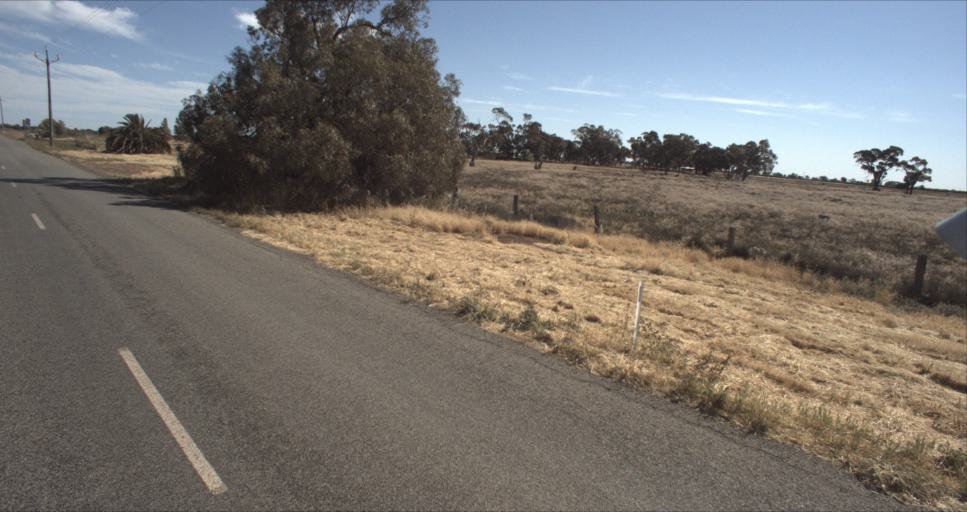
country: AU
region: New South Wales
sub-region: Leeton
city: Leeton
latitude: -34.5687
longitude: 146.3821
